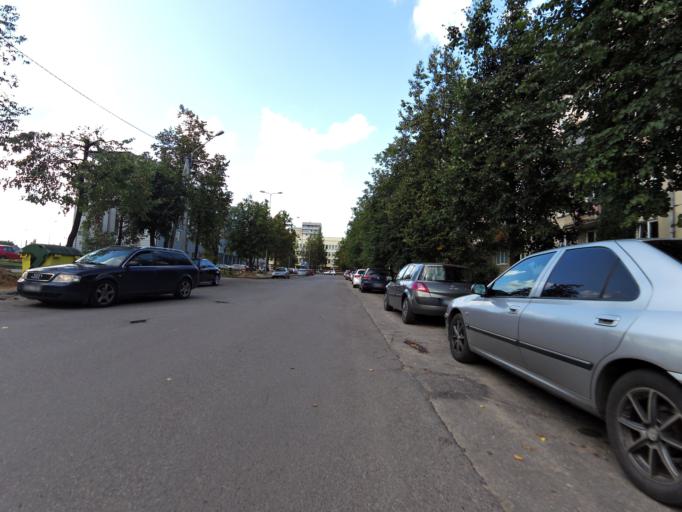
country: LT
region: Vilnius County
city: Naujamiestis
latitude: 54.6756
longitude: 25.2615
